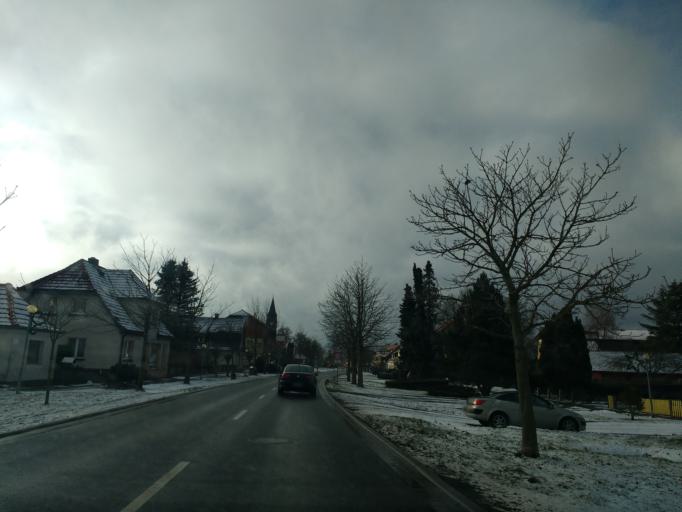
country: DE
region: Saxony-Anhalt
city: Friedrichsbrunn
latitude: 51.6902
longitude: 11.0396
